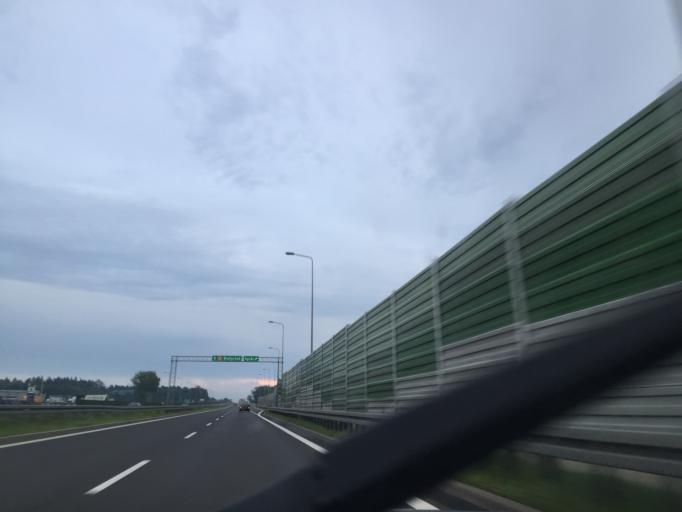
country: PL
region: Podlasie
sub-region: Powiat bialostocki
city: Choroszcz
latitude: 53.1526
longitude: 23.0360
